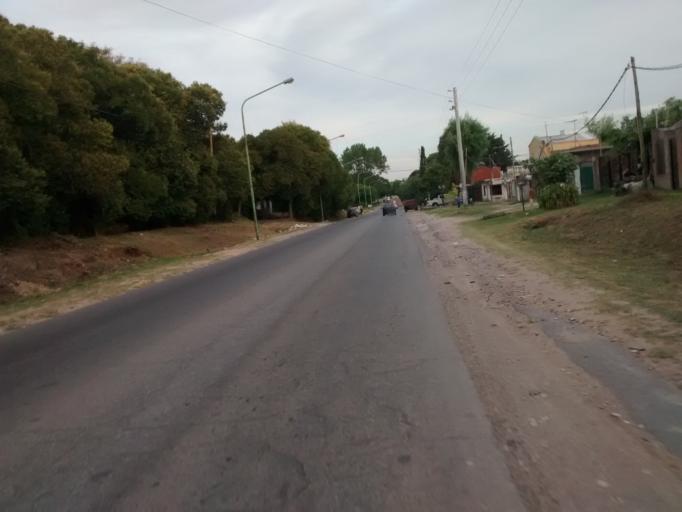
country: AR
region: Buenos Aires
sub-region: Partido de La Plata
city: La Plata
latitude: -34.9100
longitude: -58.0111
